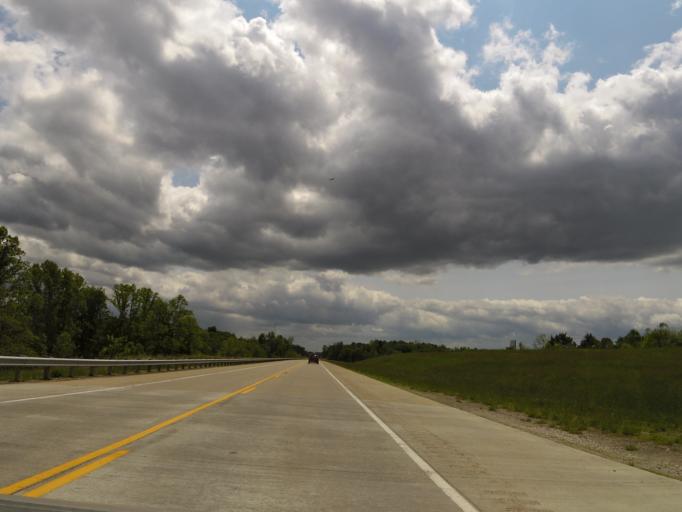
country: US
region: Ohio
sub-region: Athens County
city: Athens
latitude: 39.1893
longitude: -82.0518
